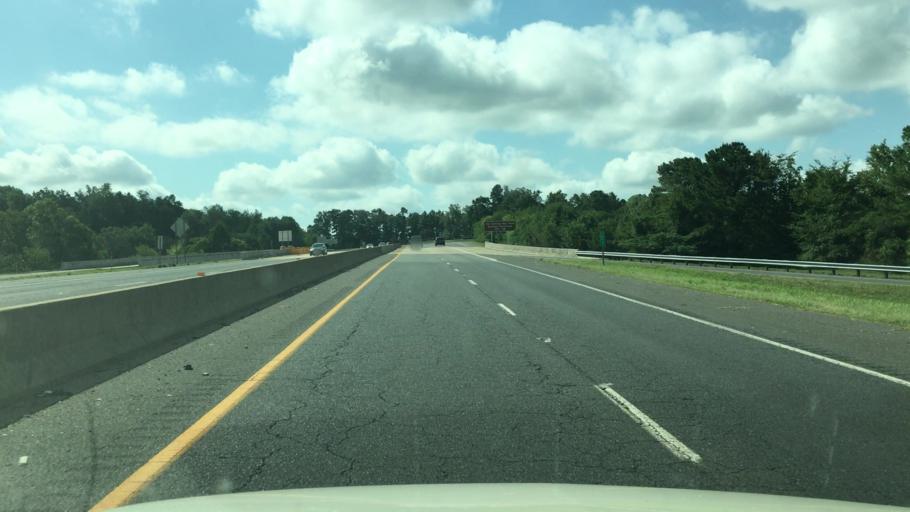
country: US
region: Arkansas
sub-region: Garland County
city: Lake Hamilton
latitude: 34.4691
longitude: -93.0887
